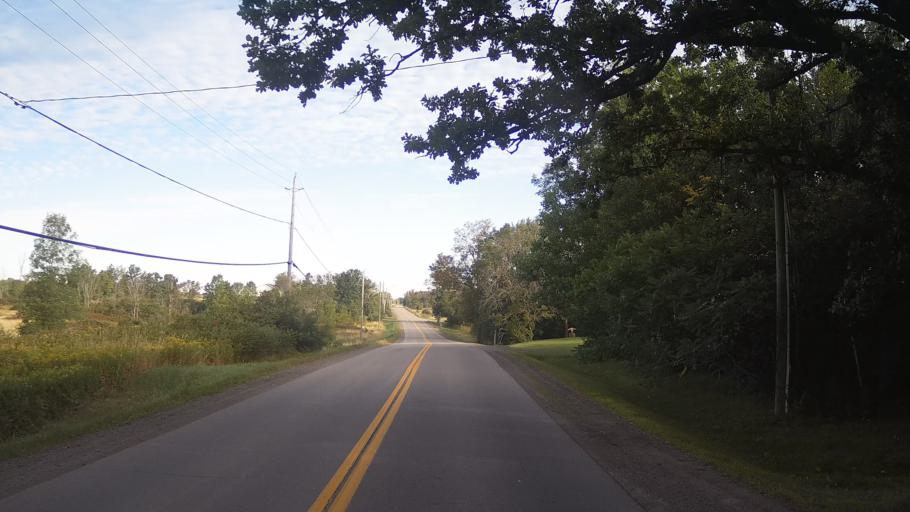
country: CA
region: Ontario
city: Gananoque
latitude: 44.3576
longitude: -76.1328
